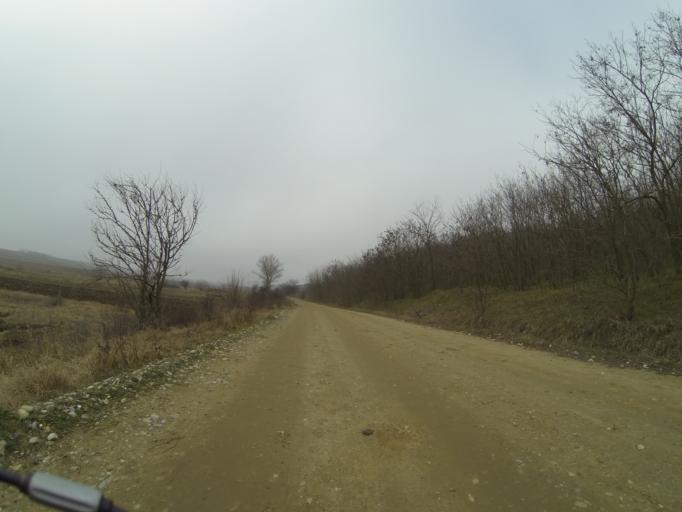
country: RO
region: Mehedinti
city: Padina Mica
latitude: 44.4868
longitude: 23.0228
